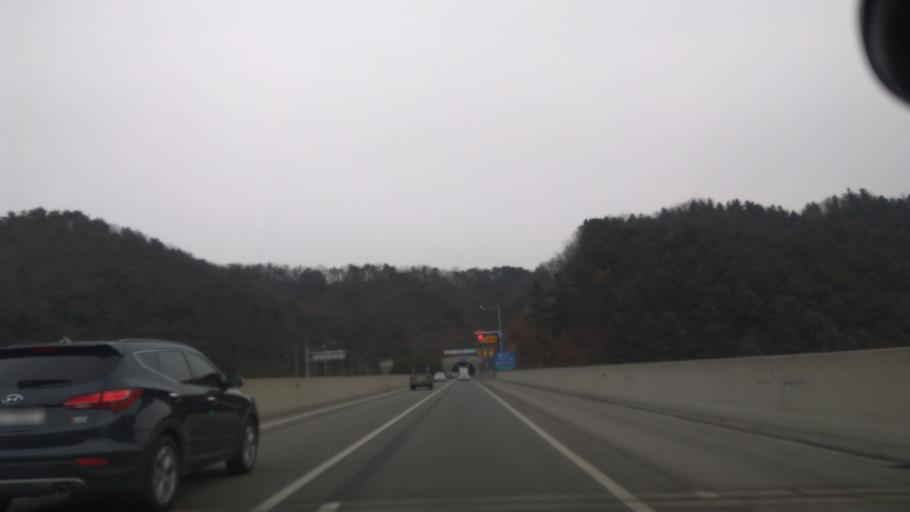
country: KR
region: Gangwon-do
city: Sindong
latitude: 37.7403
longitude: 127.6552
